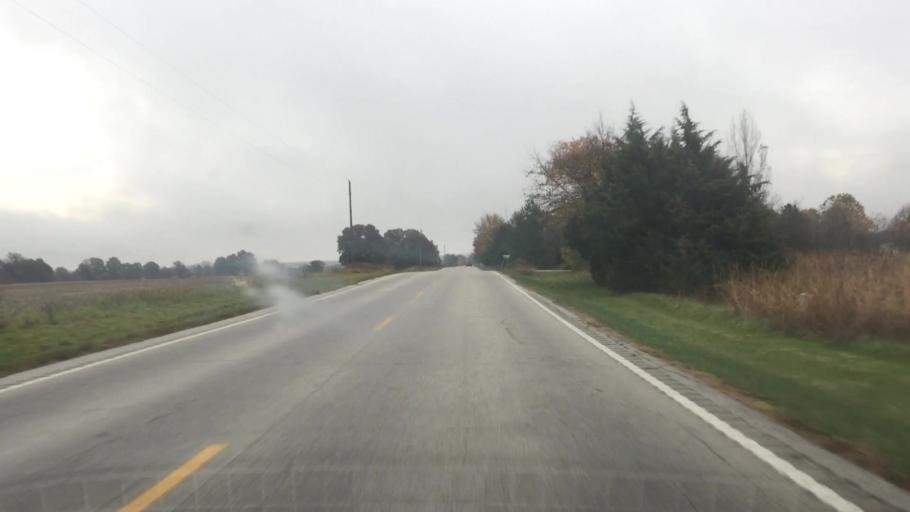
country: US
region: Missouri
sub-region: Boone County
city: Columbia
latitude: 38.9203
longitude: -92.1972
